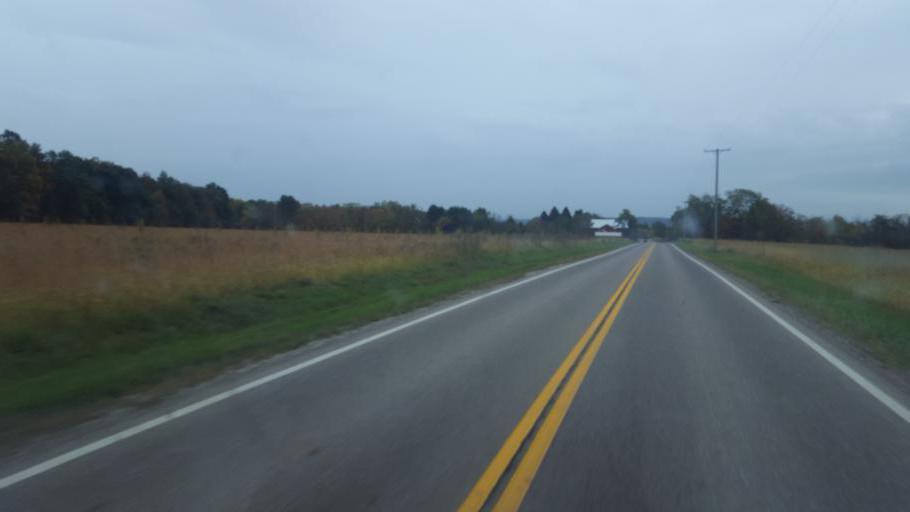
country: US
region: Ohio
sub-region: Ashland County
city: Ashland
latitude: 40.8977
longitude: -82.4171
